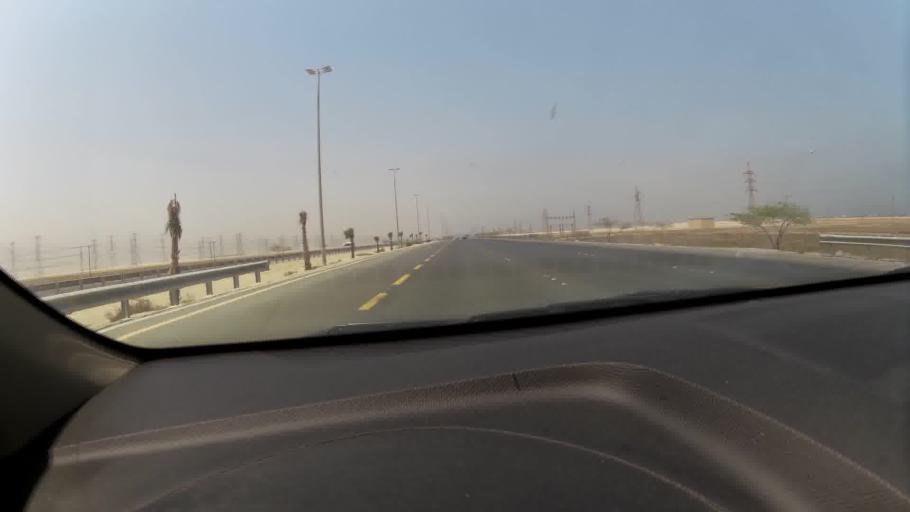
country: KW
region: Al Ahmadi
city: Al Fahahil
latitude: 28.8092
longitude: 48.2660
